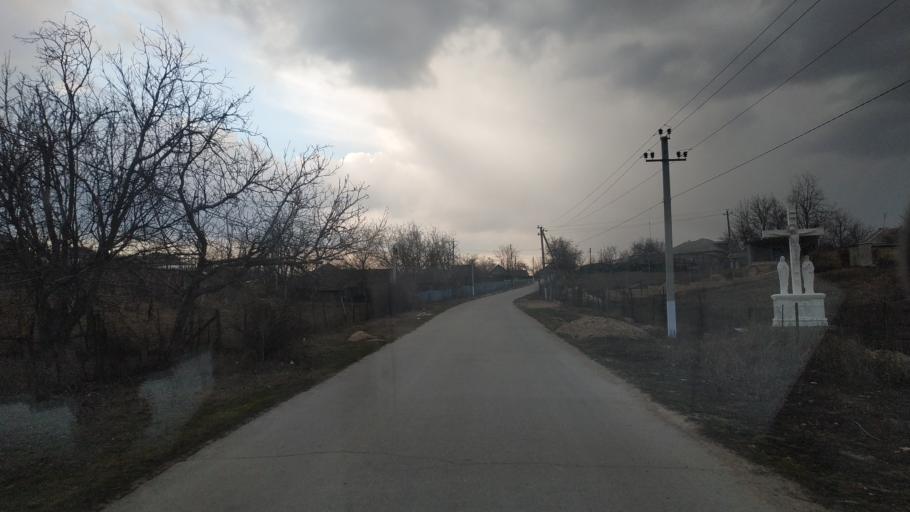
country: MD
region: Telenesti
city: Grigoriopol
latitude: 47.0251
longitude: 29.3565
